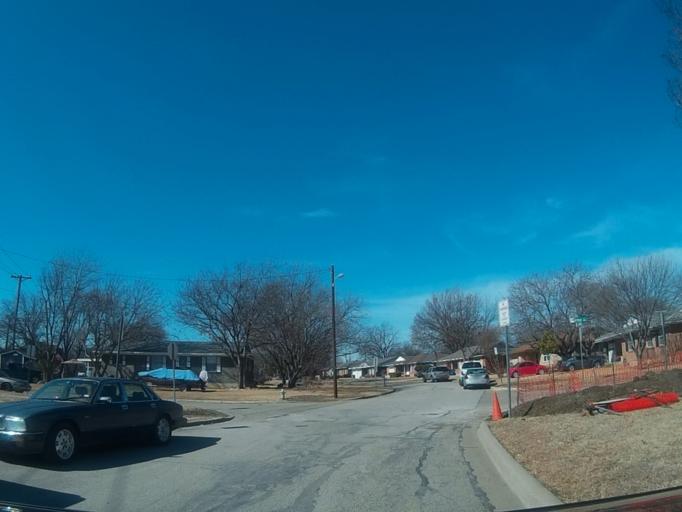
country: US
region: Texas
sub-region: Collin County
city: Allen
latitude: 33.1054
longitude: -96.6730
